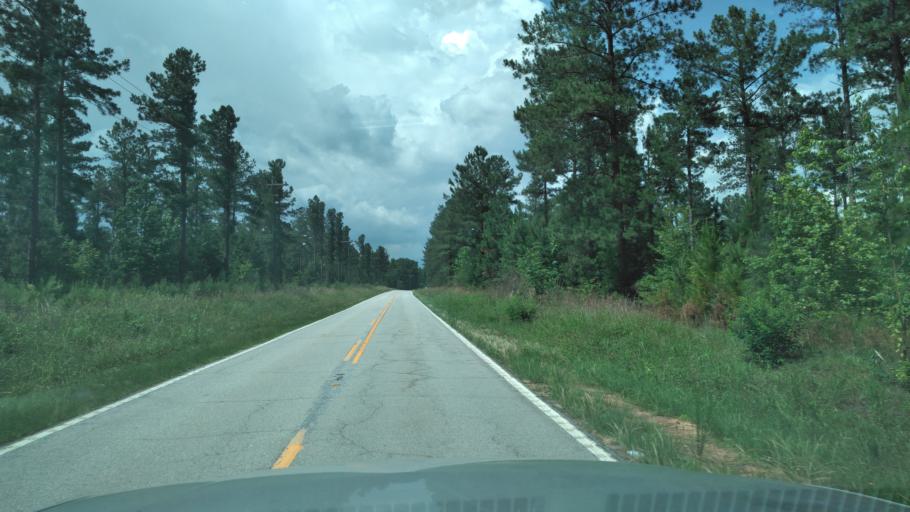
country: US
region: South Carolina
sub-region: Laurens County
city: Laurens
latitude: 34.5235
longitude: -82.0933
